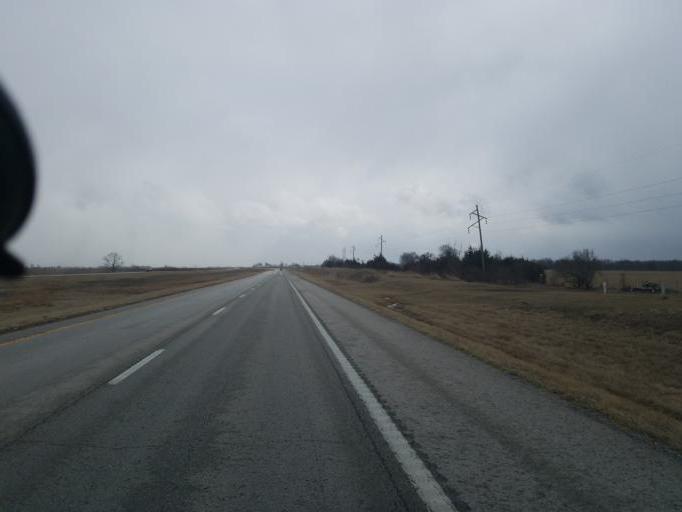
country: US
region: Missouri
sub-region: Randolph County
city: Moberly
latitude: 39.5377
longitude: -92.4485
